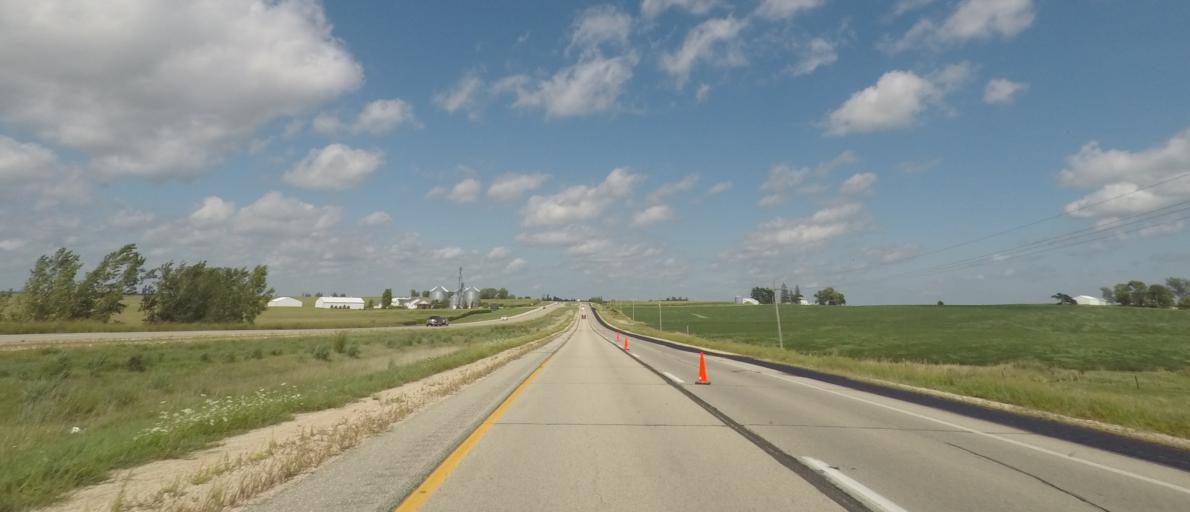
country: US
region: Iowa
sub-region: Jones County
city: Anamosa
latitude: 42.1571
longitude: -91.2365
